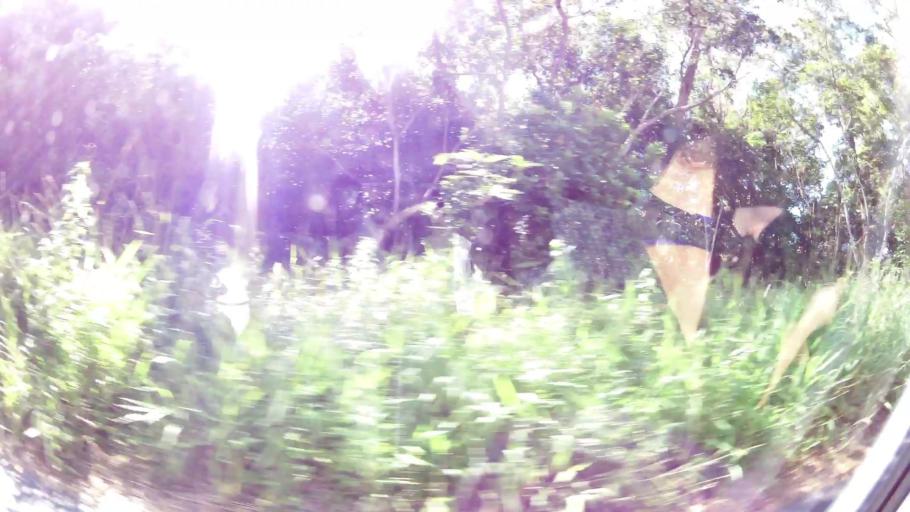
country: BN
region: Brunei and Muara
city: Bandar Seri Begawan
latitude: 4.9521
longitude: 114.9401
